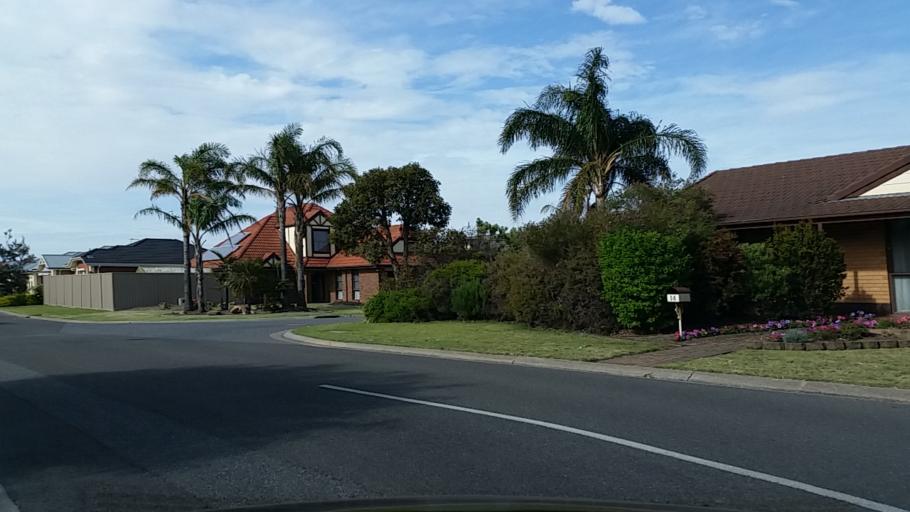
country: AU
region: South Australia
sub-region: Charles Sturt
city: Grange
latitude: -34.8971
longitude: 138.4994
